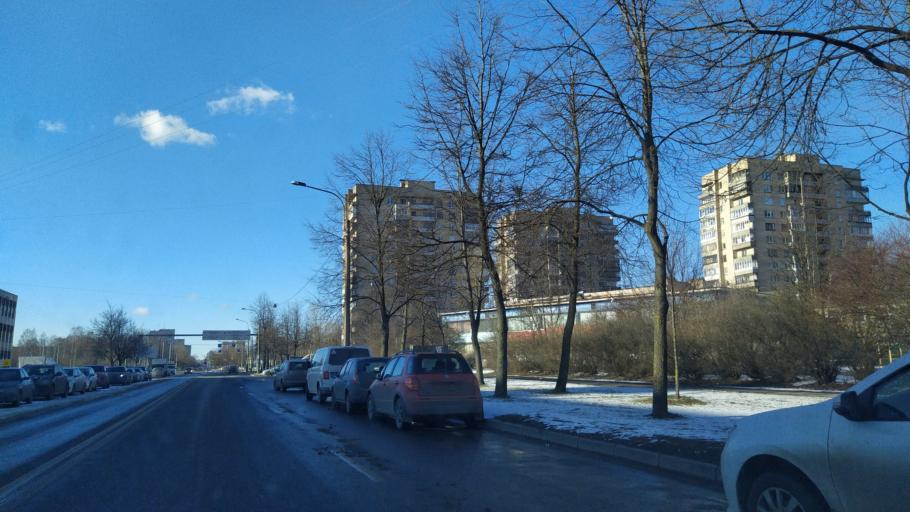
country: RU
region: Leningrad
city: Kalininskiy
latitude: 59.9725
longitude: 30.4182
